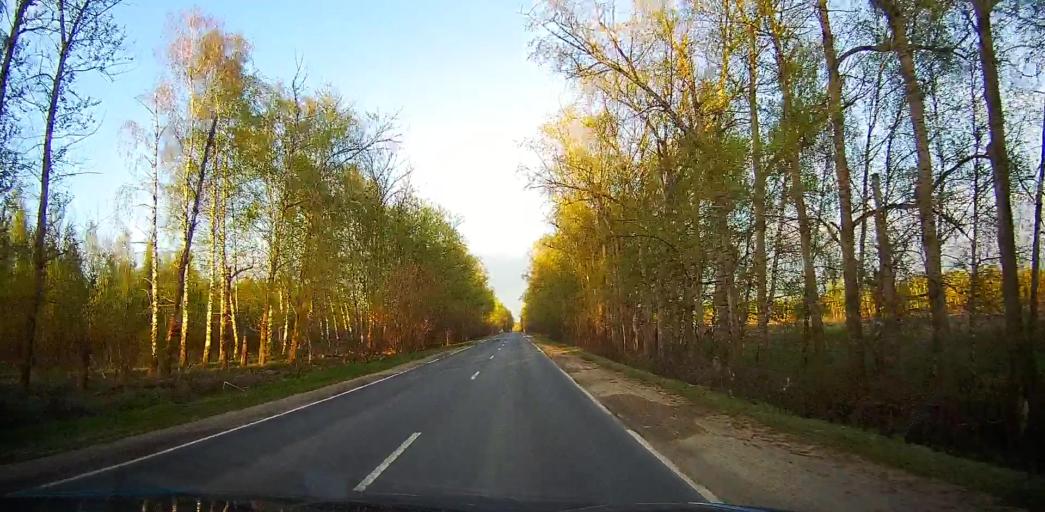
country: RU
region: Moskovskaya
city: Peski
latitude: 55.2089
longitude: 38.7182
